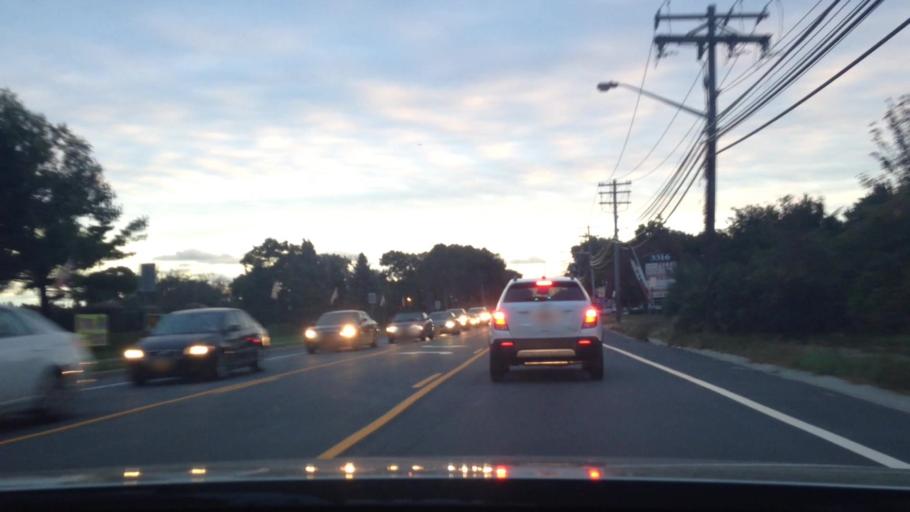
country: US
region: New York
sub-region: Suffolk County
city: Coram
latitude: 40.8447
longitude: -72.9970
